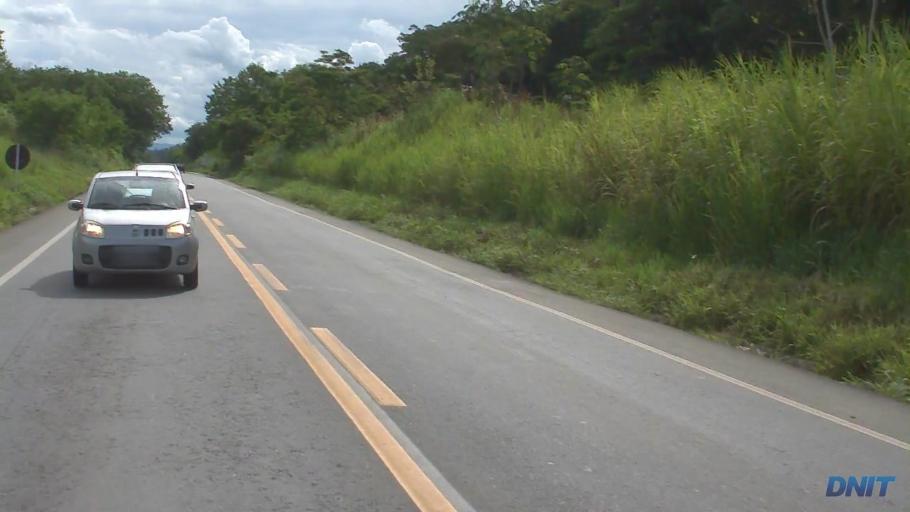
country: BR
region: Minas Gerais
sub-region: Ipaba
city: Ipaba
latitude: -19.2960
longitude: -42.3621
